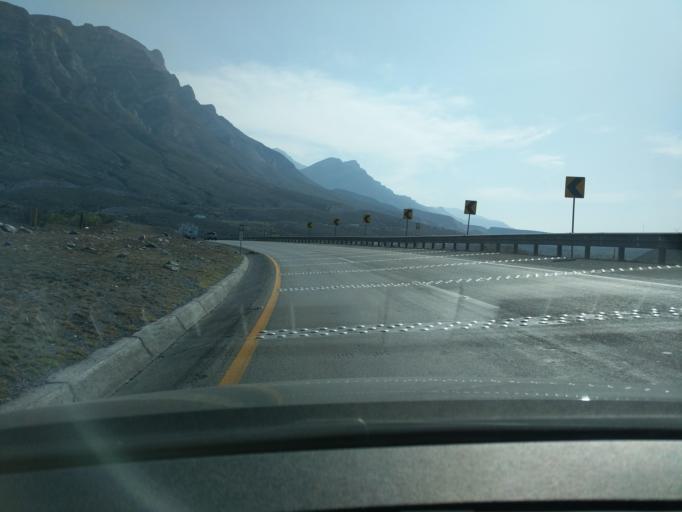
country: MX
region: Nuevo Leon
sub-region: Garcia
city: Las Torres de Guadalupe
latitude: 25.6569
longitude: -100.7195
